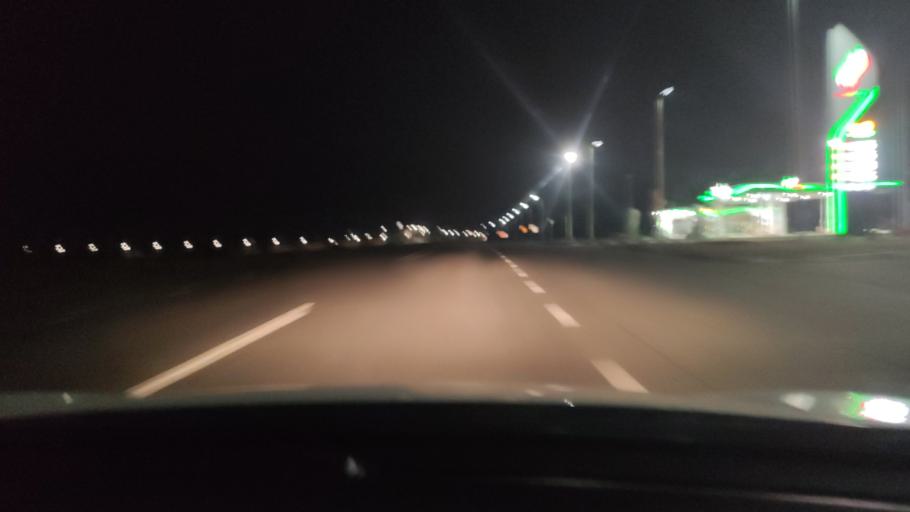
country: RU
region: Tatarstan
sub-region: Alekseyevskiy Rayon
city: Alekseyevskoye
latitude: 55.2971
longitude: 50.0437
